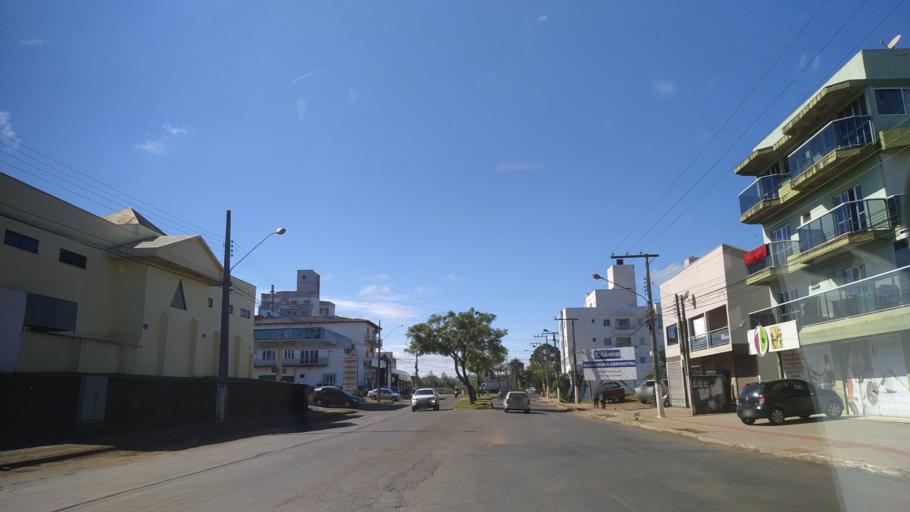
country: BR
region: Santa Catarina
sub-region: Chapeco
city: Chapeco
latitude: -27.1052
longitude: -52.6016
